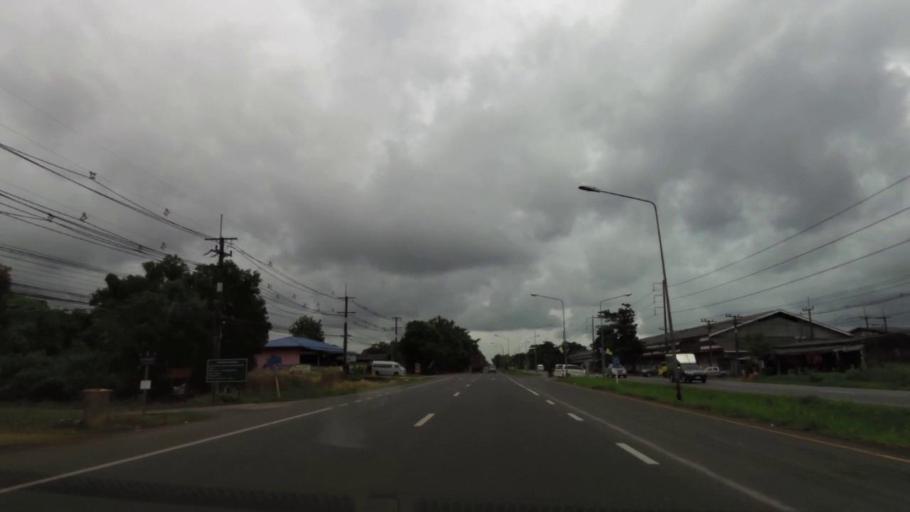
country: TH
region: Chanthaburi
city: Tha Mai
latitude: 12.6571
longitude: 102.0105
